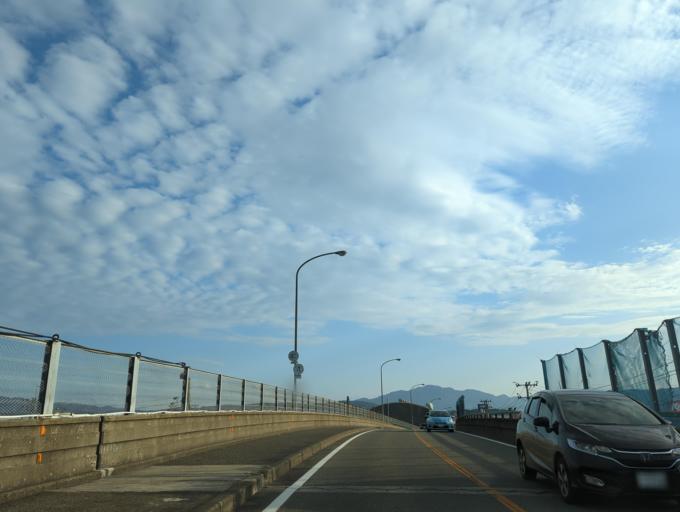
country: JP
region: Niigata
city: Kashiwazaki
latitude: 37.3654
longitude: 138.5632
